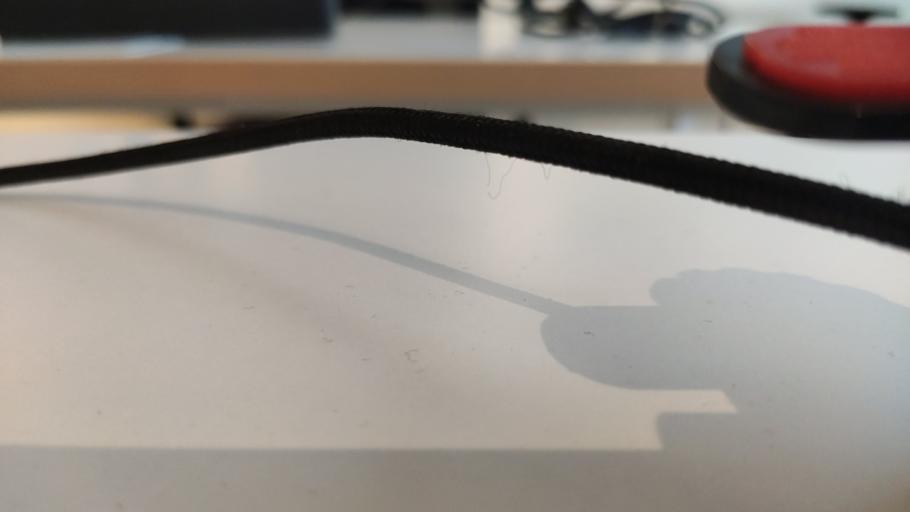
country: RU
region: Moskovskaya
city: Novopetrovskoye
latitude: 55.9697
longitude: 36.4413
